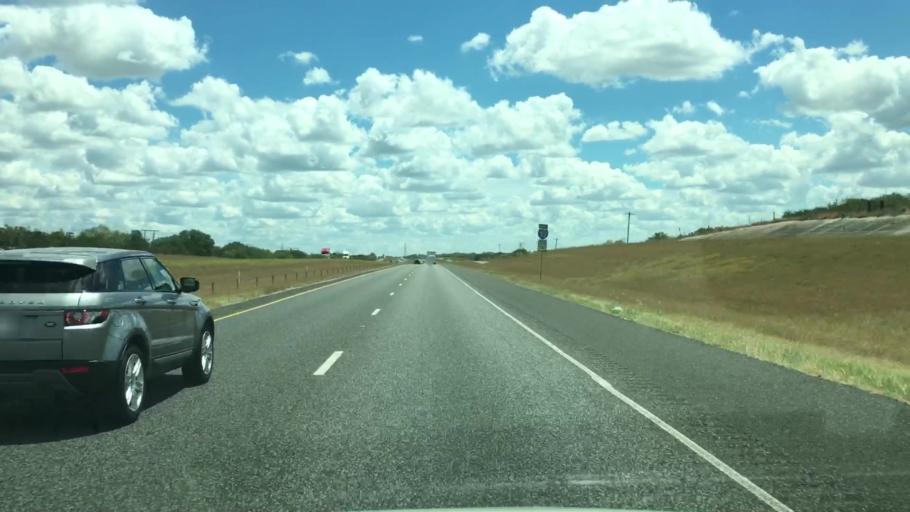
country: US
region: Texas
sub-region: Atascosa County
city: Pleasanton
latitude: 28.8387
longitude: -98.3742
